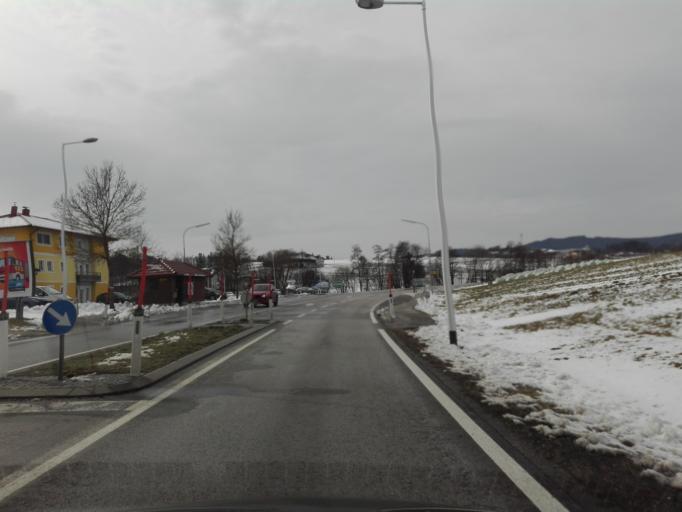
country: AT
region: Upper Austria
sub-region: Politischer Bezirk Rohrbach
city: Atzesberg
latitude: 48.4999
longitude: 13.8951
